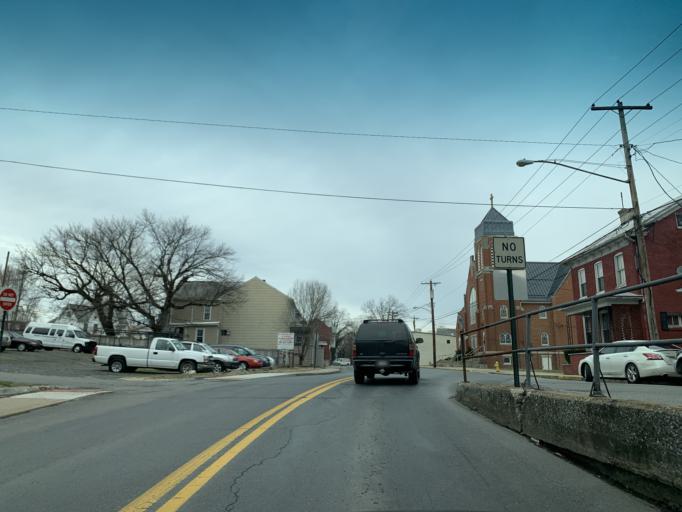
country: US
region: West Virginia
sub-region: Berkeley County
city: Martinsburg
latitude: 39.4634
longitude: -77.9616
